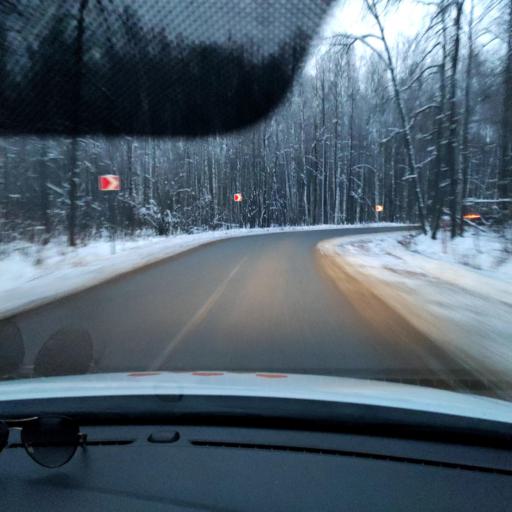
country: RU
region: Tatarstan
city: Vysokaya Gora
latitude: 55.9353
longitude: 49.1732
